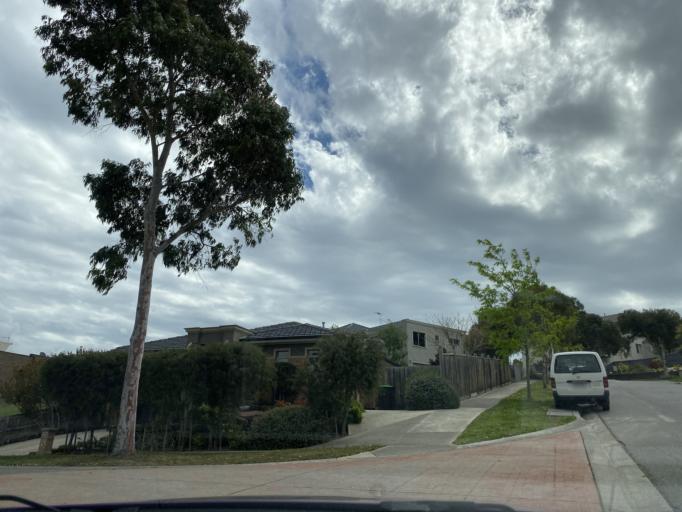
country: AU
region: Victoria
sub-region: Whittlesea
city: Mill Park
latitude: -37.6316
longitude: 145.0641
